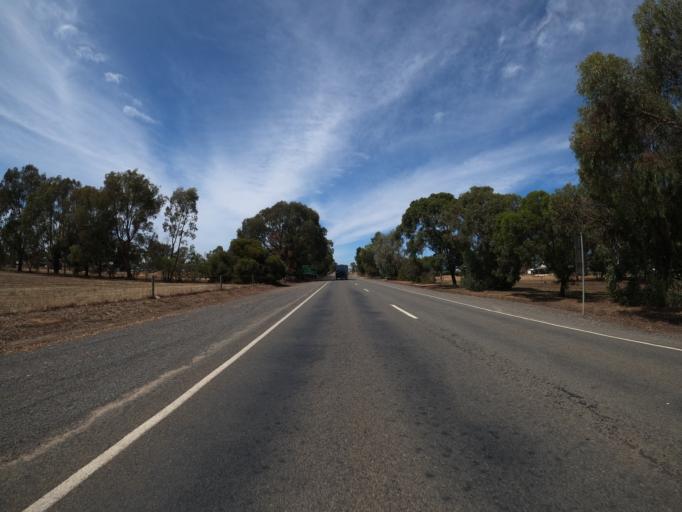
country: AU
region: Victoria
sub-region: Moira
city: Yarrawonga
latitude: -36.0385
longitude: 145.9955
